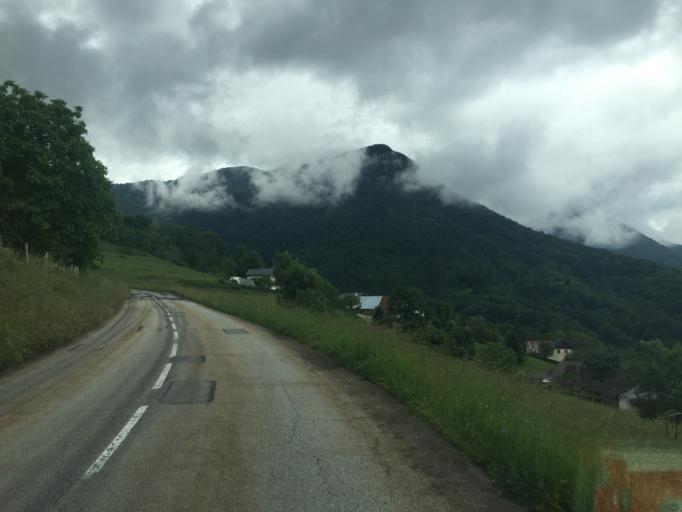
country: FR
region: Rhone-Alpes
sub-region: Departement de la Savoie
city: Barby
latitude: 45.5854
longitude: 6.0355
